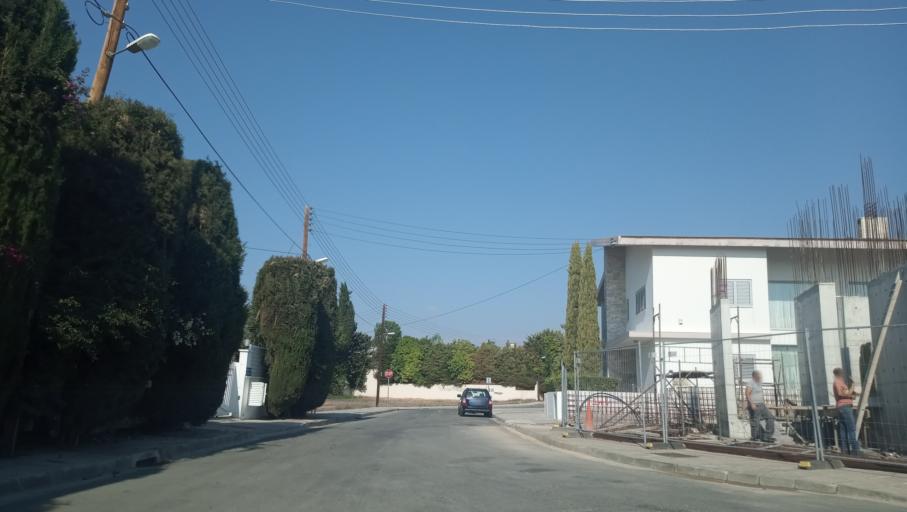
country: CY
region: Lefkosia
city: Nicosia
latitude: 35.1462
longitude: 33.3905
